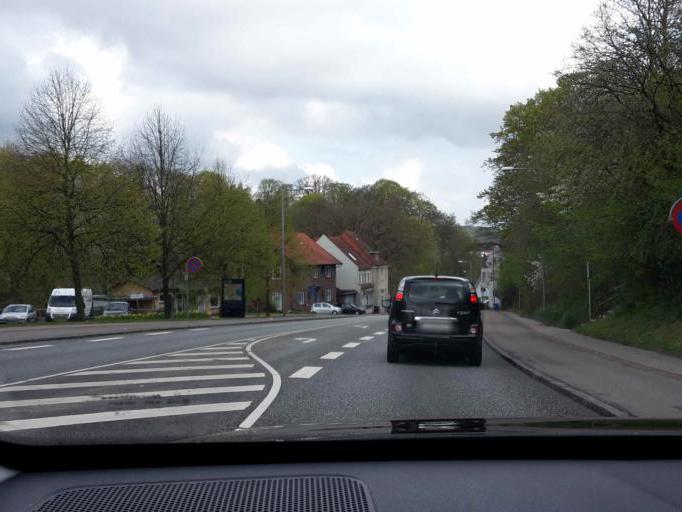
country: DK
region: South Denmark
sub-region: Vejle Kommune
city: Vejle
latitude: 55.6980
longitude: 9.5373
